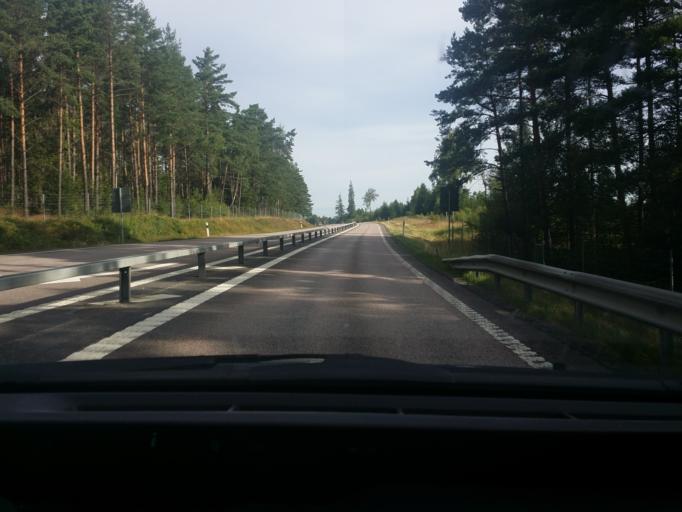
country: SE
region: Vaestmanland
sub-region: Vasteras
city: Tillberga
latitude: 59.7863
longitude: 16.5669
